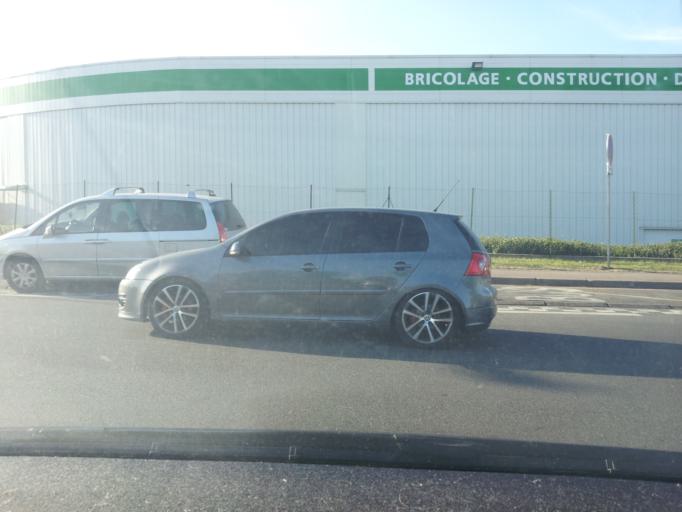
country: FR
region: Ile-de-France
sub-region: Departement de l'Essonne
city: Le Plessis-Pate
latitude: 48.6239
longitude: 2.3421
